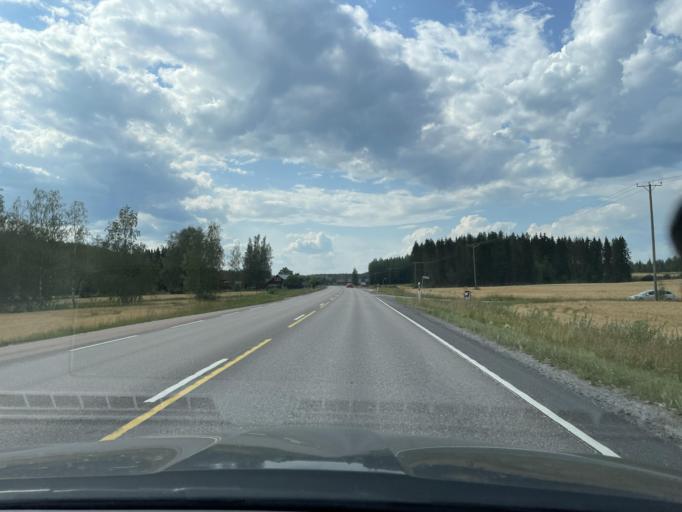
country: FI
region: Central Finland
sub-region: Jyvaeskylae
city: Korpilahti
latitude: 61.9920
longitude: 25.4521
